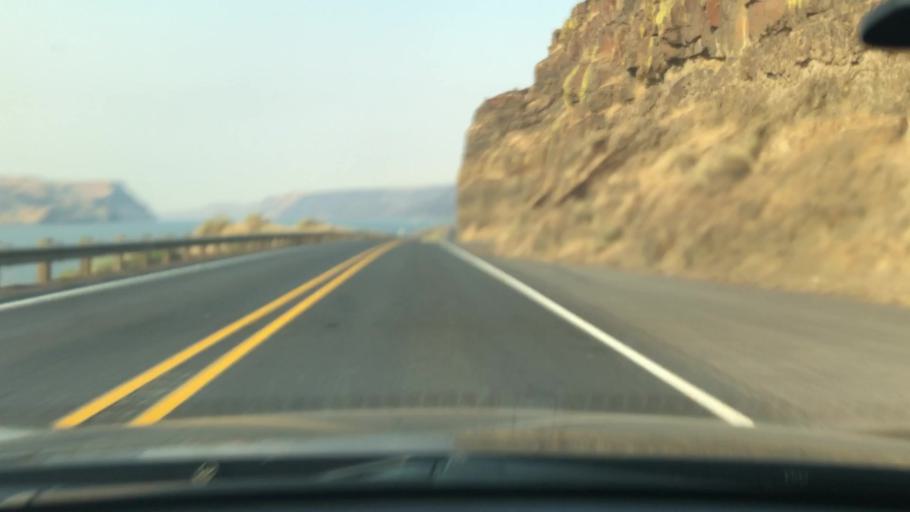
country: US
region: Washington
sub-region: Benton County
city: Highland
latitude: 45.9506
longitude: -119.0591
